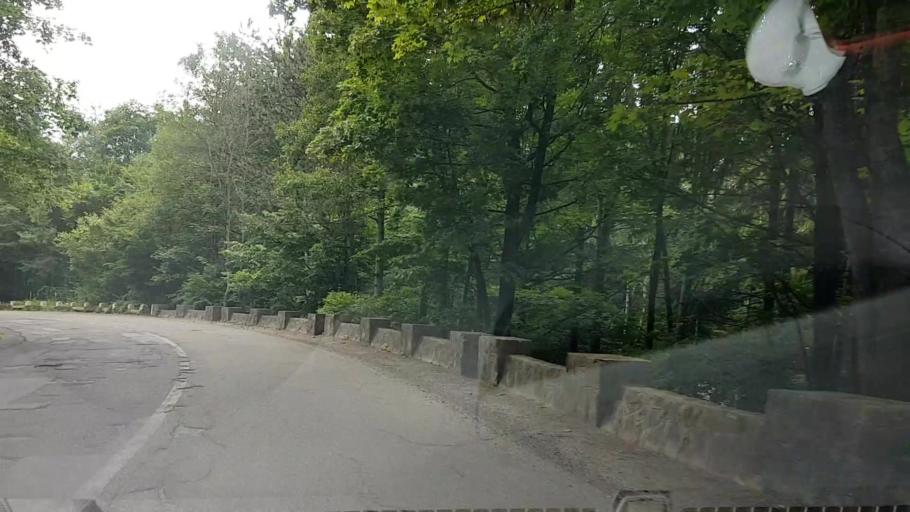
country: RO
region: Neamt
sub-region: Comuna Bicaz
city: Dodeni
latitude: 46.9395
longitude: 26.1160
